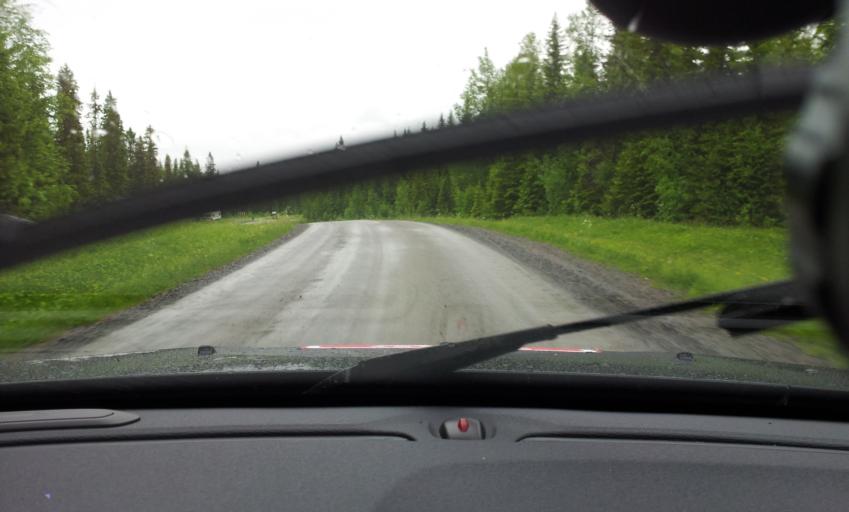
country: SE
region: Jaemtland
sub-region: Are Kommun
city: Are
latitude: 63.4305
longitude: 12.8025
